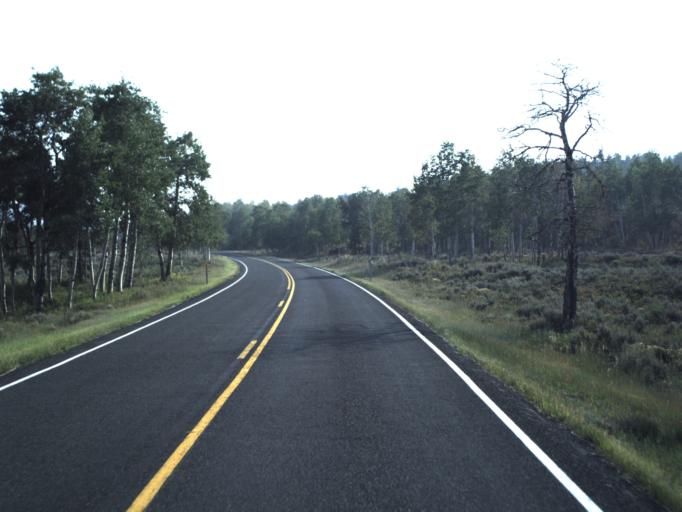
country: US
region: Wyoming
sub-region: Uinta County
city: Evanston
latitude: 40.8695
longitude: -110.8375
